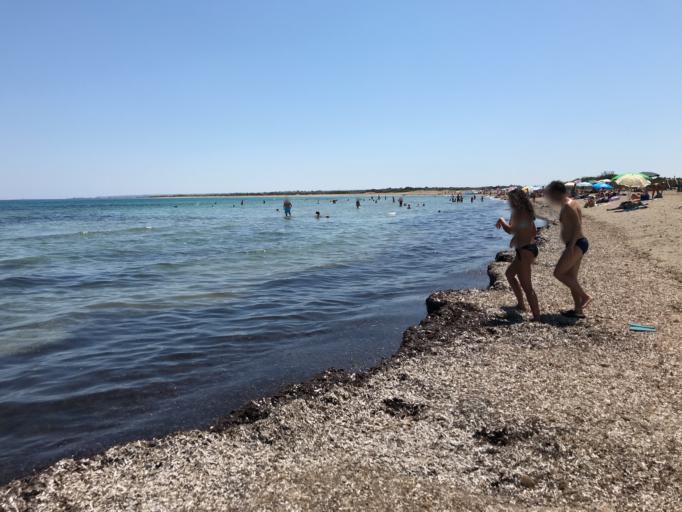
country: IT
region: Sicily
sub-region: Provincia di Siracusa
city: Pachino
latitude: 36.8022
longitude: 15.0953
